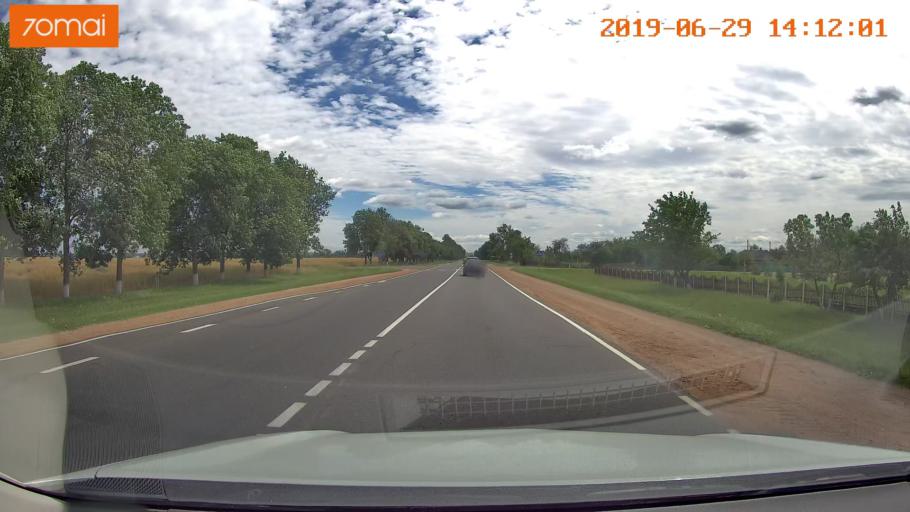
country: BY
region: Minsk
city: Salihorsk
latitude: 52.8140
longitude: 27.5057
